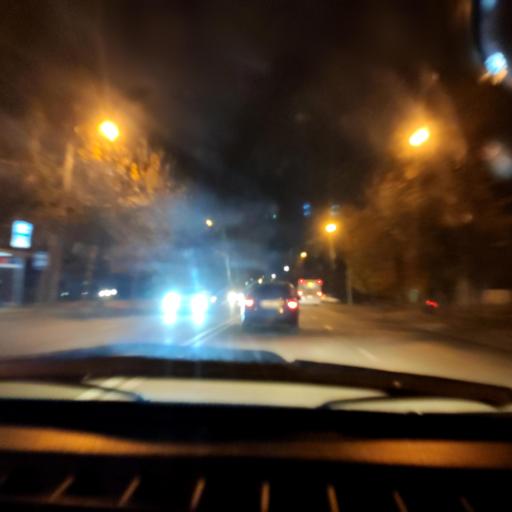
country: RU
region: Bashkortostan
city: Ufa
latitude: 54.7459
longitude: 56.0258
